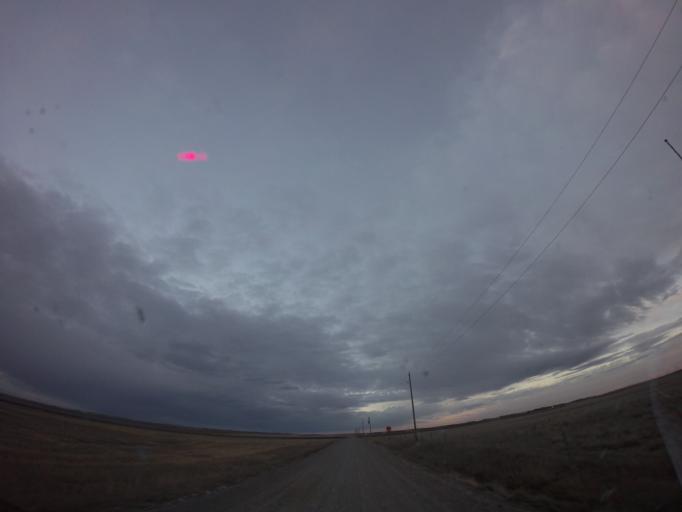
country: US
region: Montana
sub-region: Yellowstone County
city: Billings
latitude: 45.9436
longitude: -108.7100
